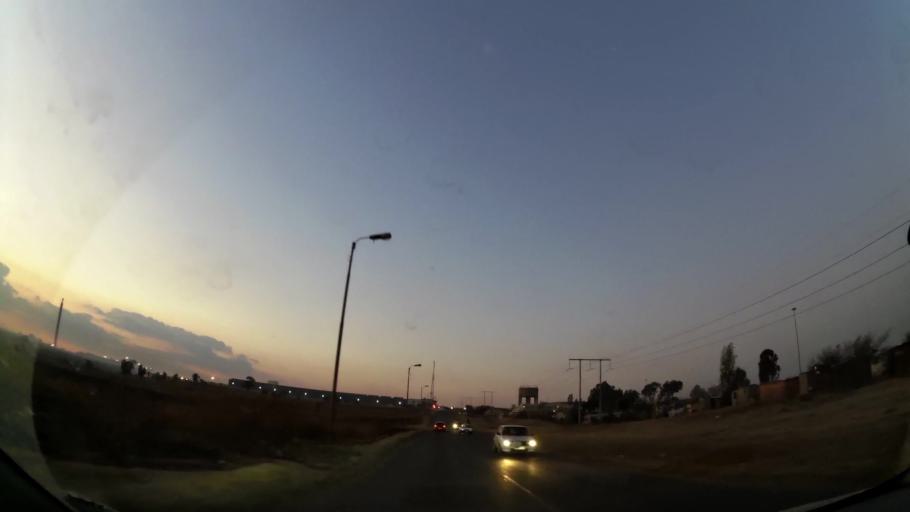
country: ZA
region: Gauteng
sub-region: Ekurhuleni Metropolitan Municipality
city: Springs
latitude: -26.2939
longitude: 28.3830
